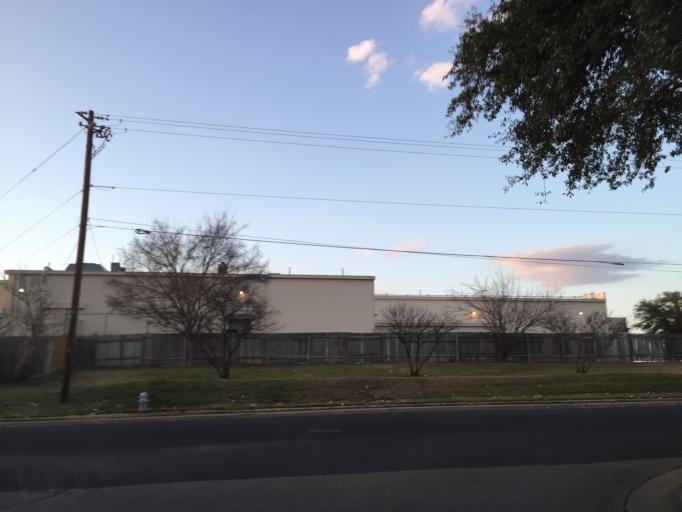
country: US
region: Texas
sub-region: Williamson County
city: Jollyville
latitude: 30.4408
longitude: -97.7420
